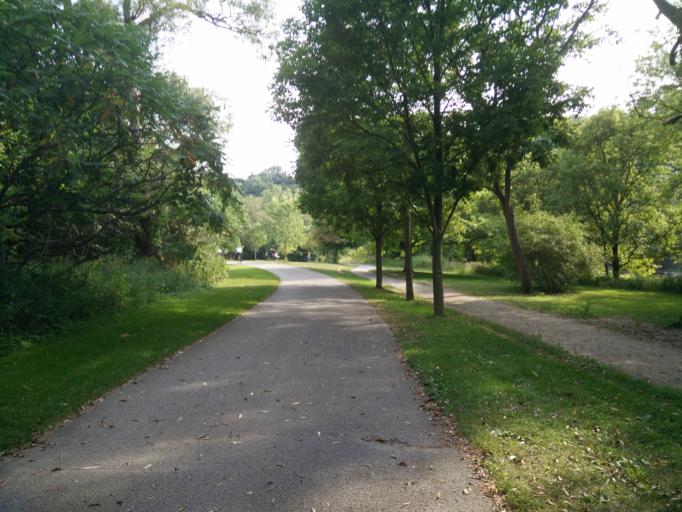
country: CA
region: Ontario
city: Etobicoke
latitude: 43.6549
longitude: -79.5022
